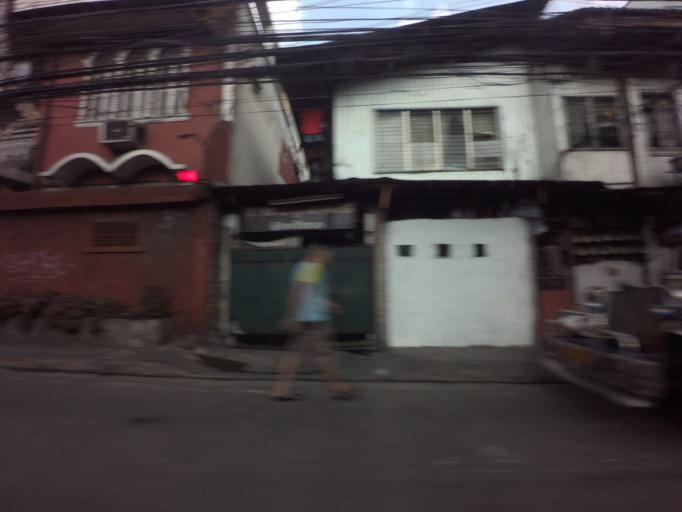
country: PH
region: Metro Manila
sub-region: Mandaluyong
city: Mandaluyong City
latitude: 14.5663
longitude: 121.0472
